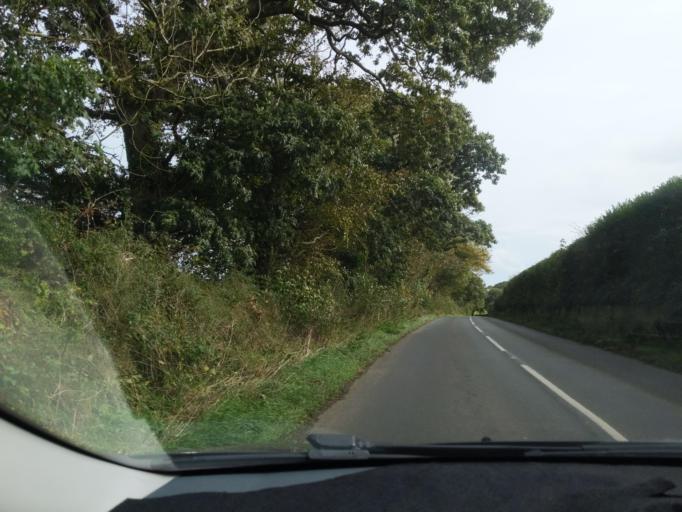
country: GB
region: England
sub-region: Cornwall
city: Mevagissey
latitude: 50.2482
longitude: -4.8168
